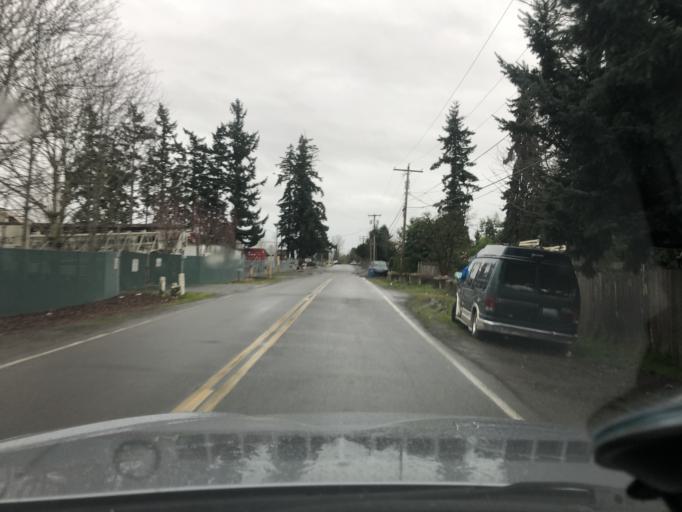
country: US
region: Washington
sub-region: King County
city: Kent
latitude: 47.3669
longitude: -122.2351
